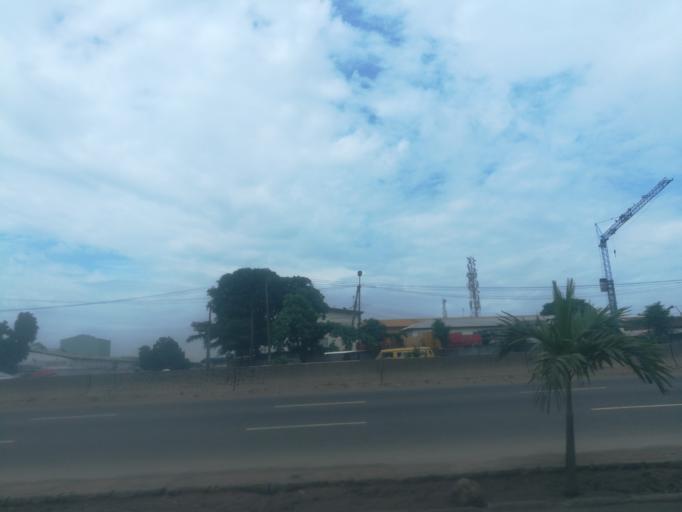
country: NG
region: Lagos
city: Somolu
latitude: 6.5518
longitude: 3.3754
